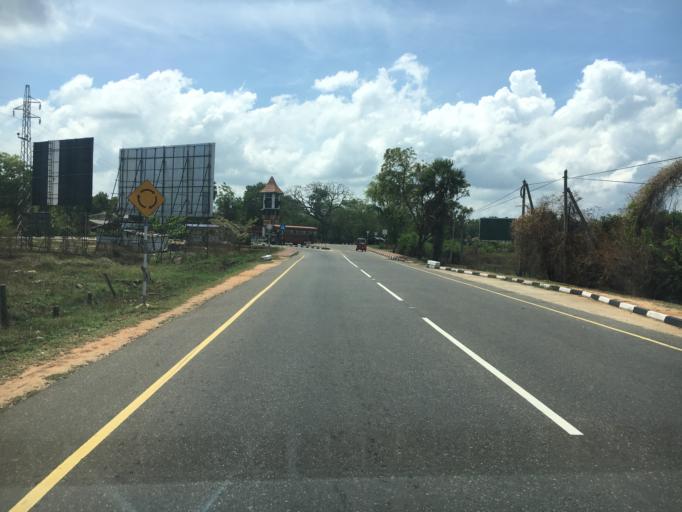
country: LK
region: North Central
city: Anuradhapura
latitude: 8.2748
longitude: 80.4995
